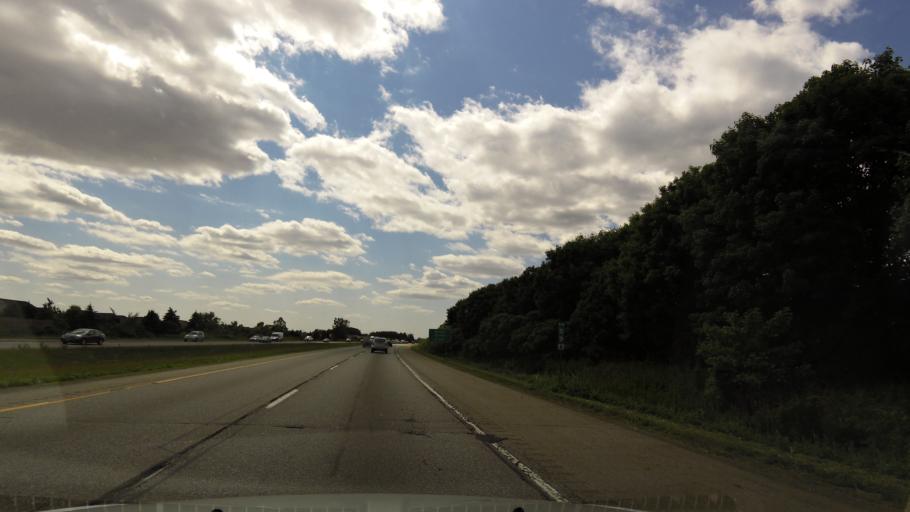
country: CA
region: Ontario
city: Ancaster
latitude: 43.2048
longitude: -79.9879
